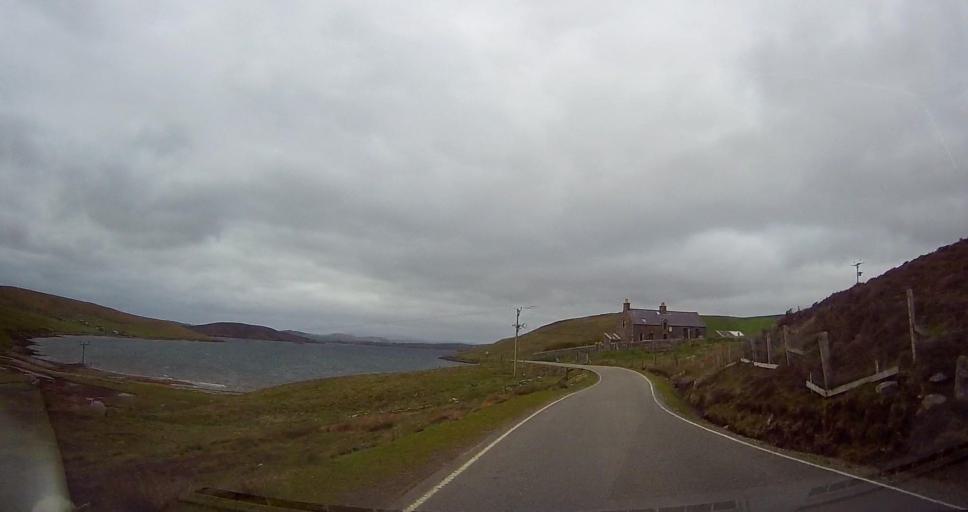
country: GB
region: Scotland
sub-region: Shetland Islands
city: Lerwick
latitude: 60.3325
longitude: -1.3354
